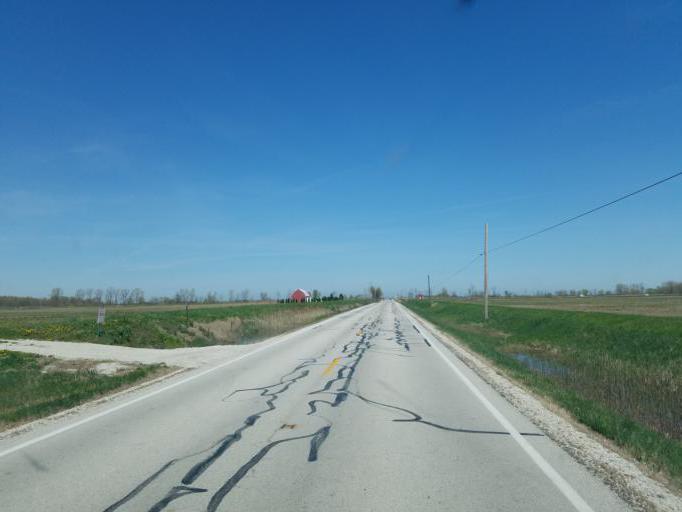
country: US
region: Ohio
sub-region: Ottawa County
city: Oak Harbor
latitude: 41.5977
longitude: -83.1451
